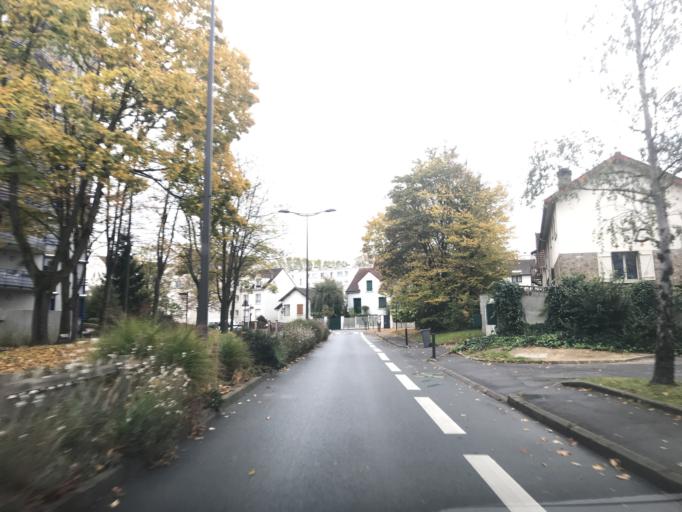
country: FR
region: Ile-de-France
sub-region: Departement de l'Essonne
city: Verrieres-le-Buisson
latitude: 48.7333
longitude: 2.2633
